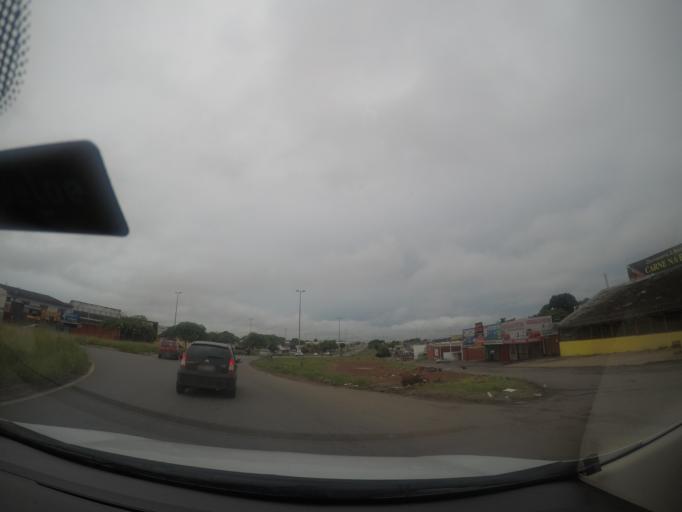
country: BR
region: Goias
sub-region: Aparecida De Goiania
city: Aparecida de Goiania
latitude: -16.7606
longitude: -49.3444
